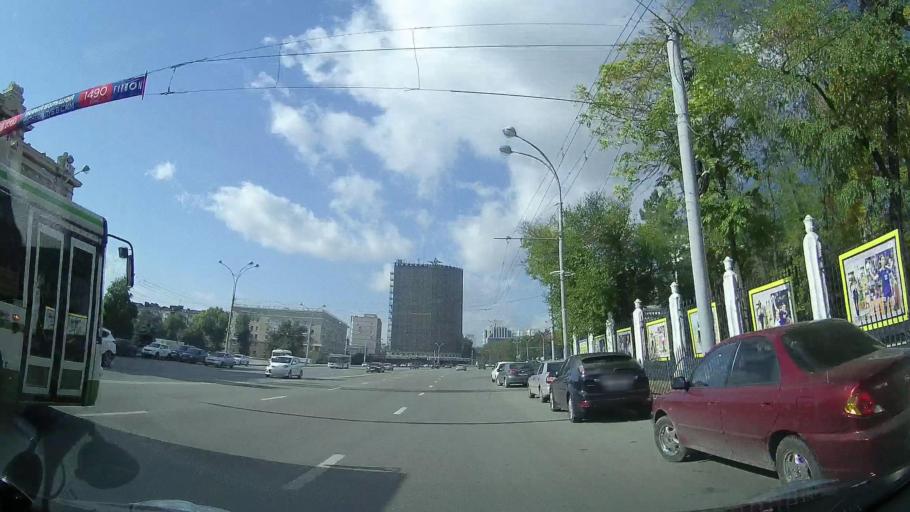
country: RU
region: Rostov
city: Rostov-na-Donu
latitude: 47.2278
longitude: 39.7467
